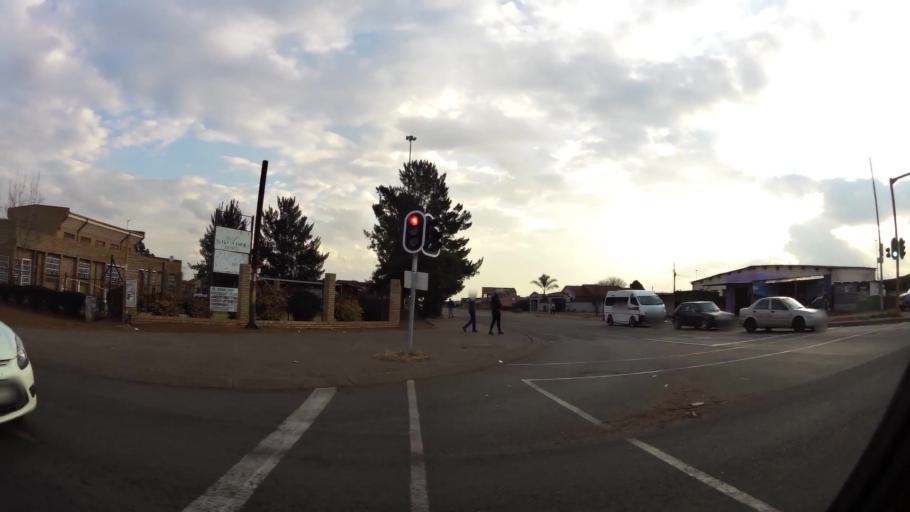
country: ZA
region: Gauteng
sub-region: City of Johannesburg Metropolitan Municipality
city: Orange Farm
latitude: -26.5825
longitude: 27.8434
